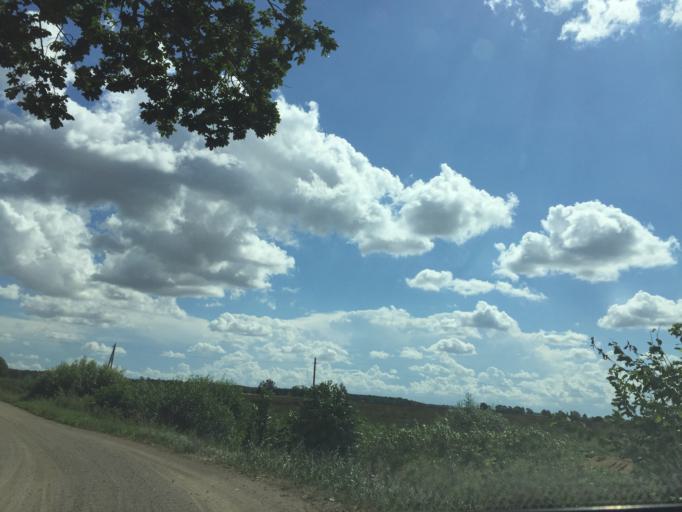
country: LV
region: Rundales
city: Pilsrundale
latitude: 56.3226
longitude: 23.9874
